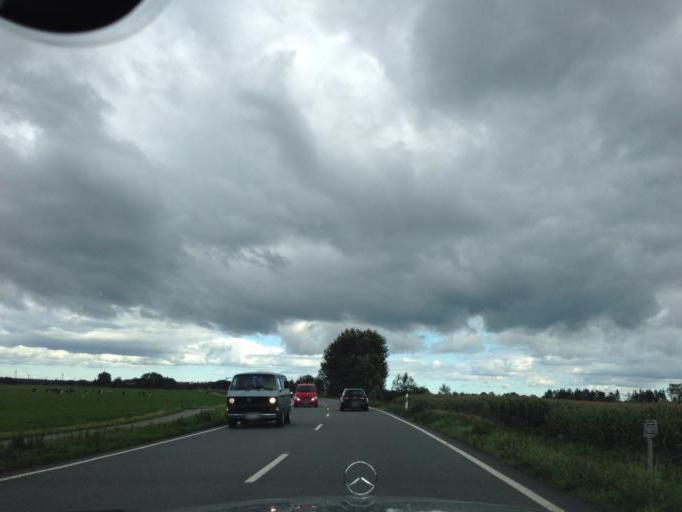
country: DE
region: Schleswig-Holstein
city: Stadum
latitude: 54.7416
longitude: 9.0613
